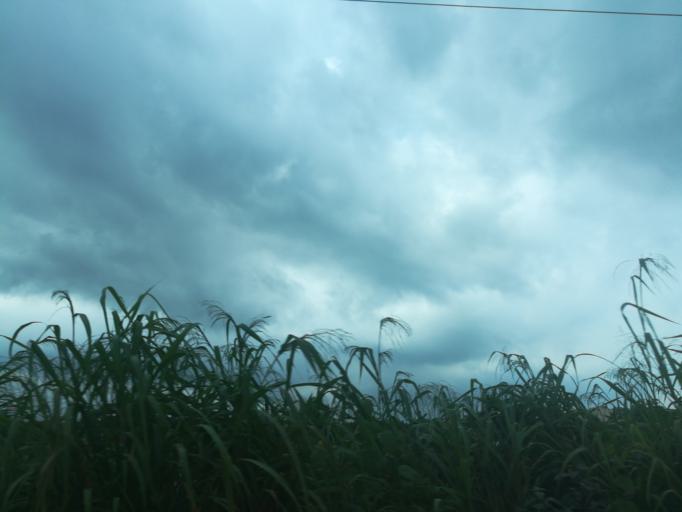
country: NG
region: Lagos
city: Ikorodu
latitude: 6.6642
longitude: 3.6042
